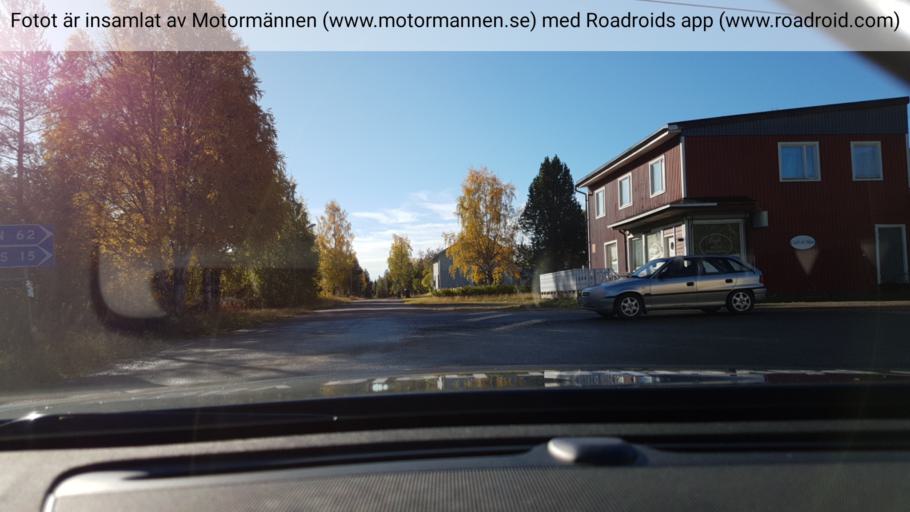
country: SE
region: Norrbotten
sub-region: Alvsbyns Kommun
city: AElvsbyn
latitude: 66.2777
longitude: 21.1228
